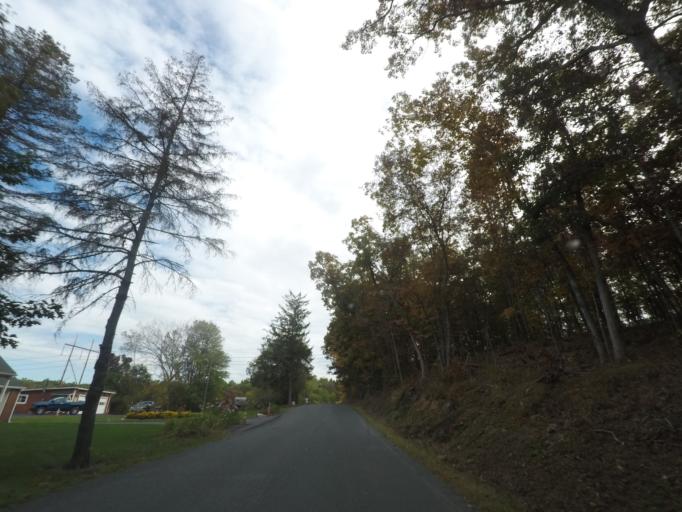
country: US
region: New York
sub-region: Rensselaer County
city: Nassau
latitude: 42.5481
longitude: -73.6345
